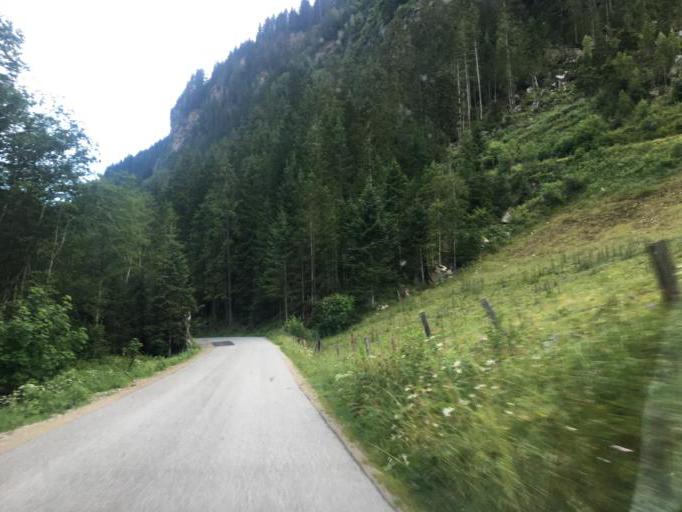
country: AT
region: Styria
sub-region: Politischer Bezirk Liezen
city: Haus
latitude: 47.3388
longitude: 13.7420
